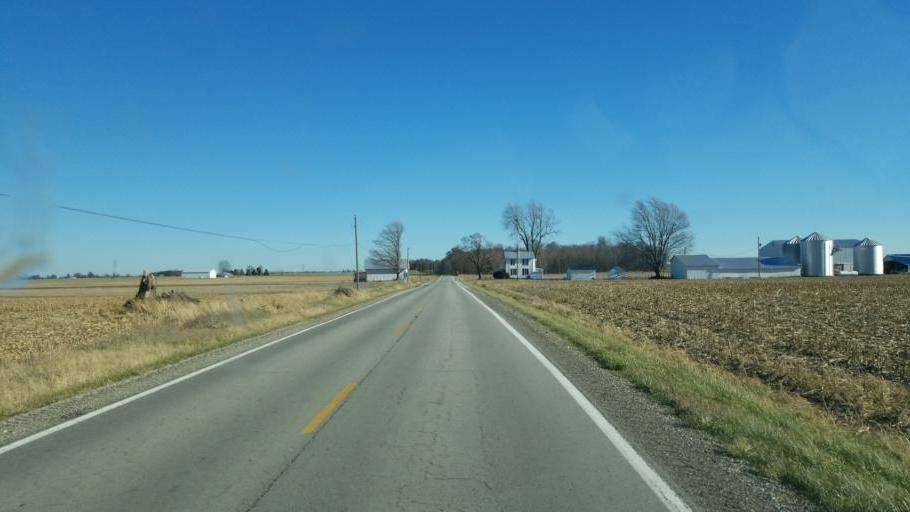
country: US
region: Ohio
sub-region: Crawford County
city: Crestline
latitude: 40.9021
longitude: -82.8074
